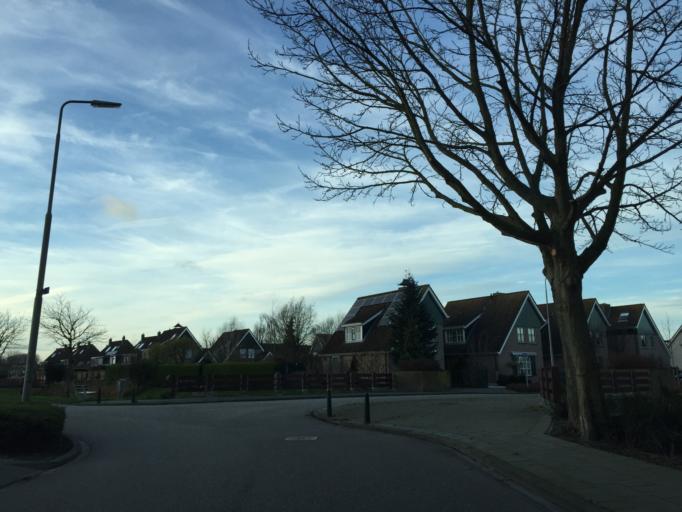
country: NL
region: North Brabant
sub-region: Gemeente Steenbergen
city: Steenbergen
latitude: 51.5908
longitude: 4.3319
